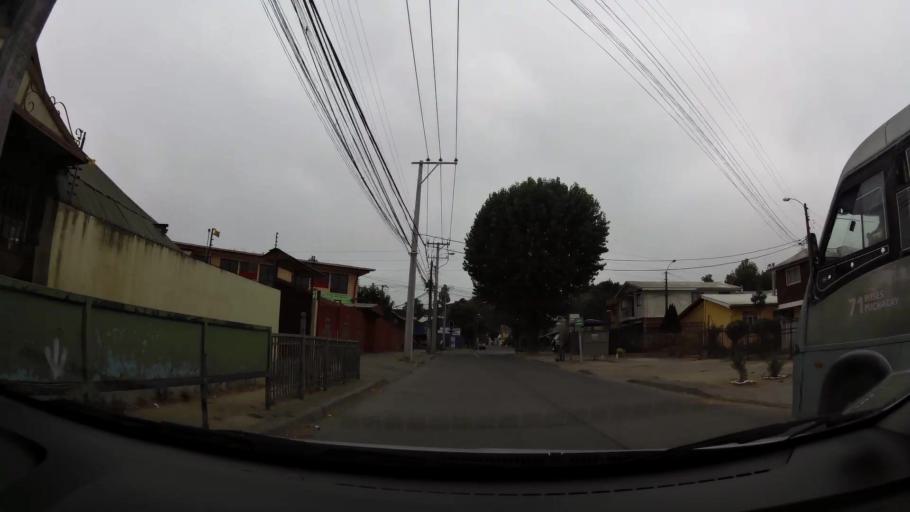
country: CL
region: Biobio
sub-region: Provincia de Concepcion
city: Concepcion
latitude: -36.8144
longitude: -73.0384
